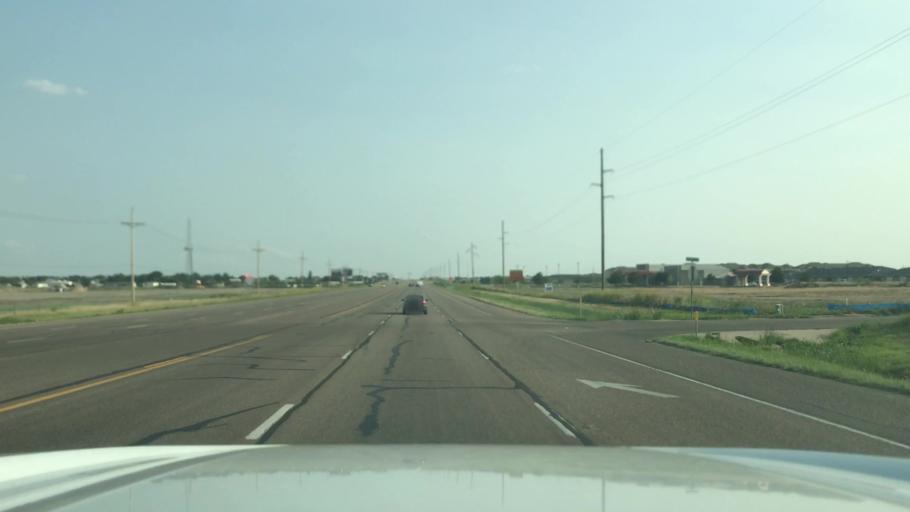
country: US
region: Texas
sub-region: Potter County
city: Amarillo
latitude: 35.1372
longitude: -101.9382
